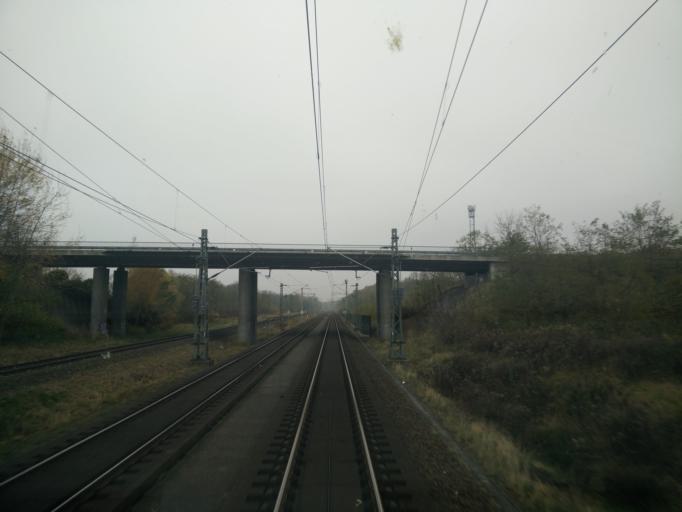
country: DE
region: Brandenburg
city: Pawesin
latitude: 52.5832
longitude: 12.7687
